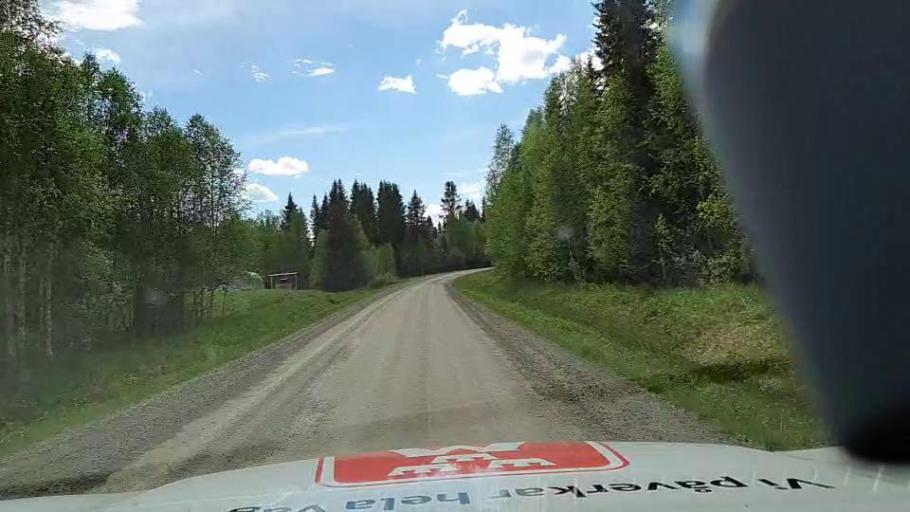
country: SE
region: Vaesterbotten
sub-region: Vilhelmina Kommun
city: Sjoberg
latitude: 64.5469
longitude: 15.7915
